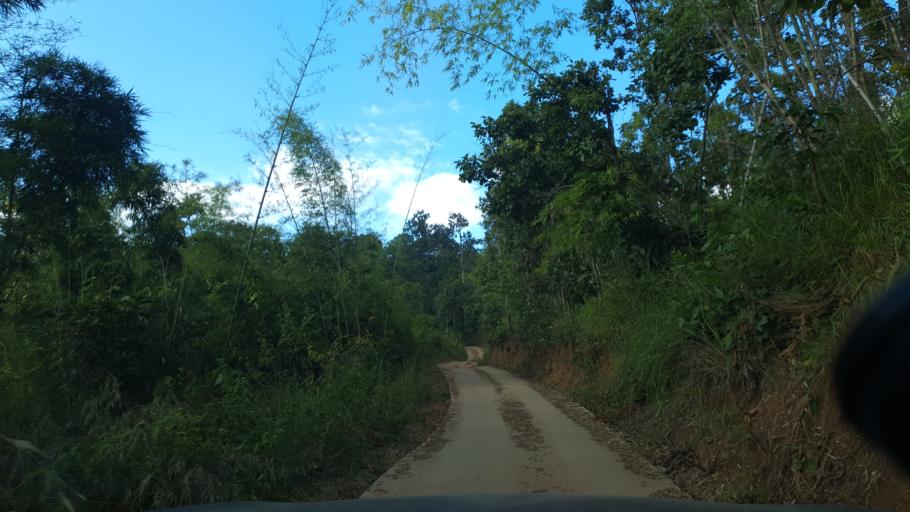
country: TH
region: Chiang Mai
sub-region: Amphoe Chiang Dao
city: Chiang Dao
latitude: 19.4089
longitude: 98.8325
